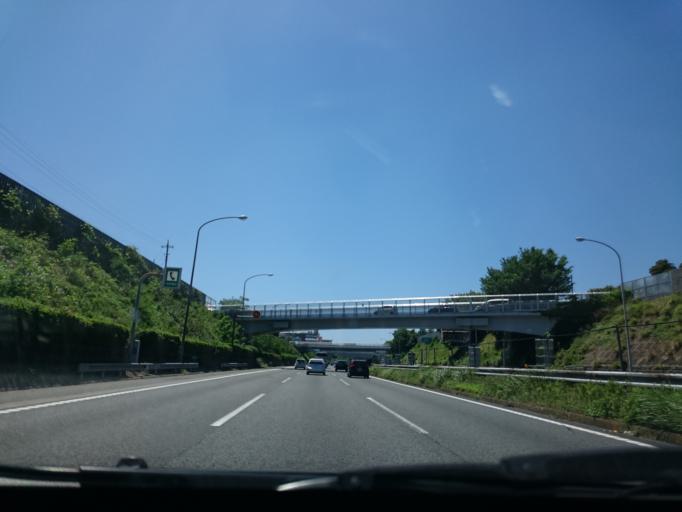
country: JP
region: Kanagawa
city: Minami-rinkan
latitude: 35.4729
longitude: 139.4472
